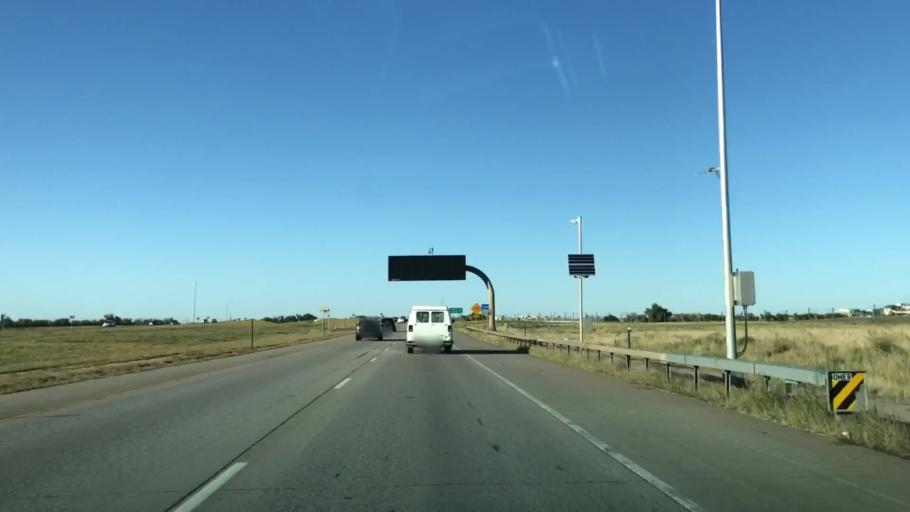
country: US
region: Colorado
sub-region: Adams County
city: Aurora
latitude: 39.7917
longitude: -104.7882
